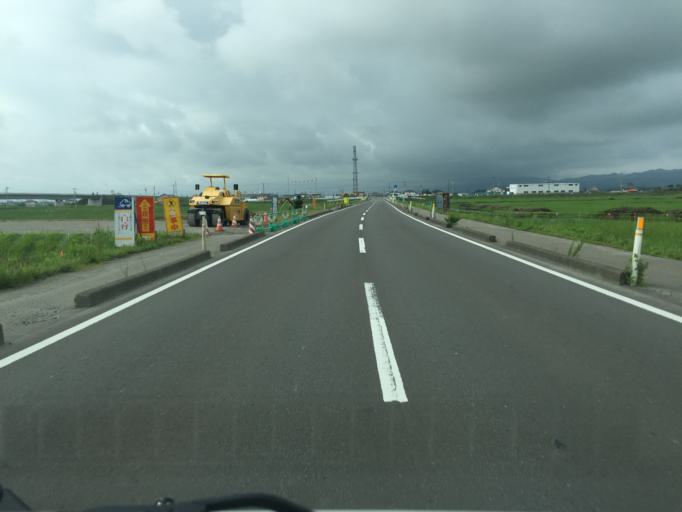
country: JP
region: Miyagi
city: Watari
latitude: 38.0375
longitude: 140.8896
